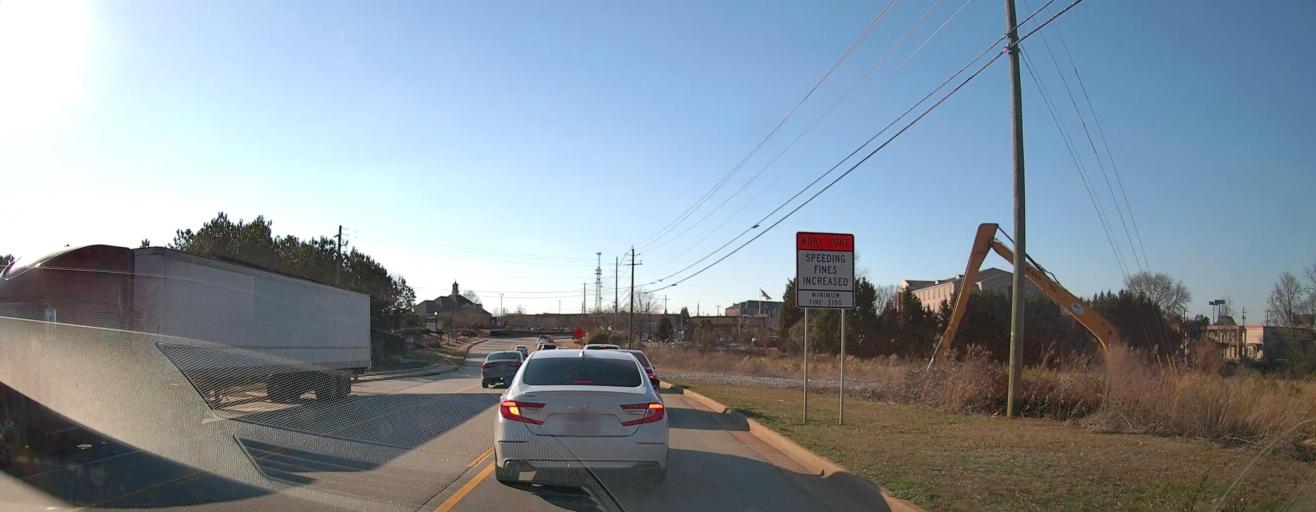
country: US
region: Georgia
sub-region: Henry County
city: McDonough
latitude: 33.4235
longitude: -84.1815
